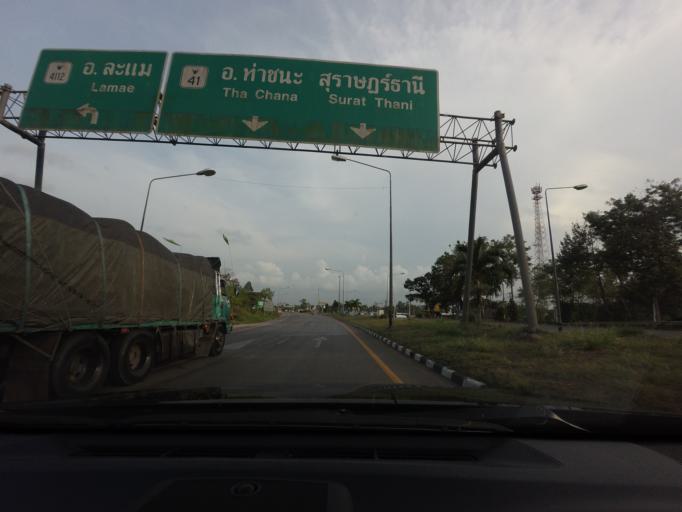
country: TH
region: Chumphon
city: Lamae
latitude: 9.7657
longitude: 99.0793
